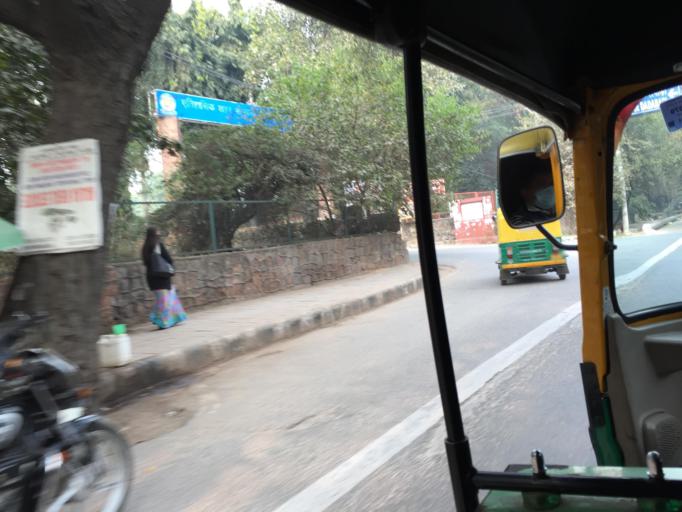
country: IN
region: NCT
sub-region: New Delhi
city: New Delhi
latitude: 28.5147
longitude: 77.1868
